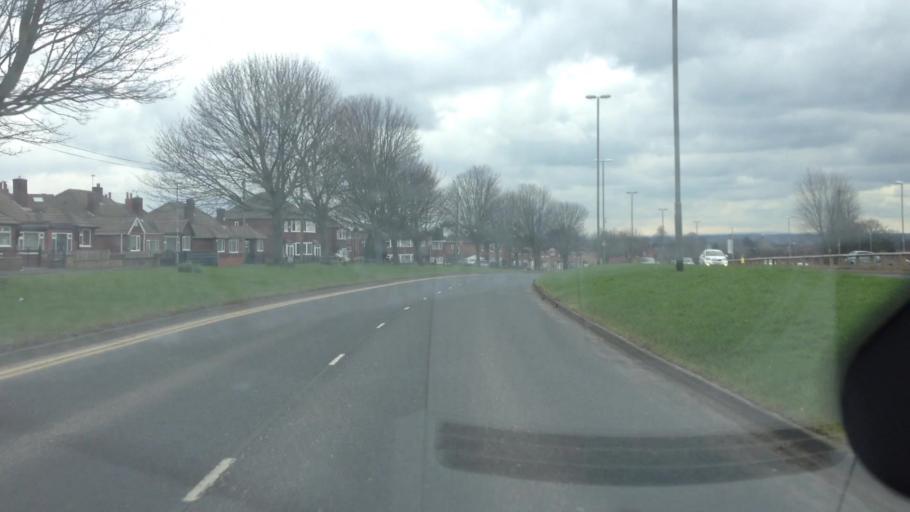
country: GB
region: England
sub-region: City and Borough of Leeds
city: Scholes
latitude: 53.8129
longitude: -1.4564
